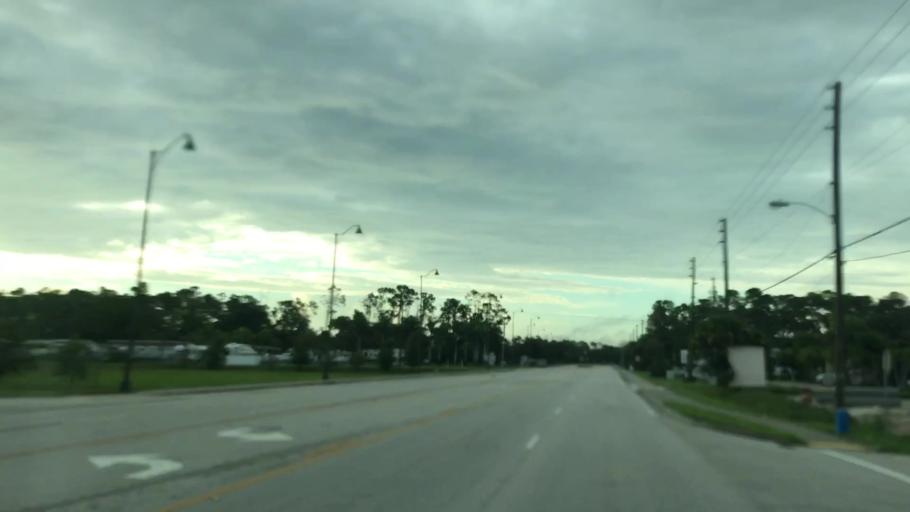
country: US
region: Florida
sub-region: Lee County
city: Bonita Springs
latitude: 26.3568
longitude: -81.7846
